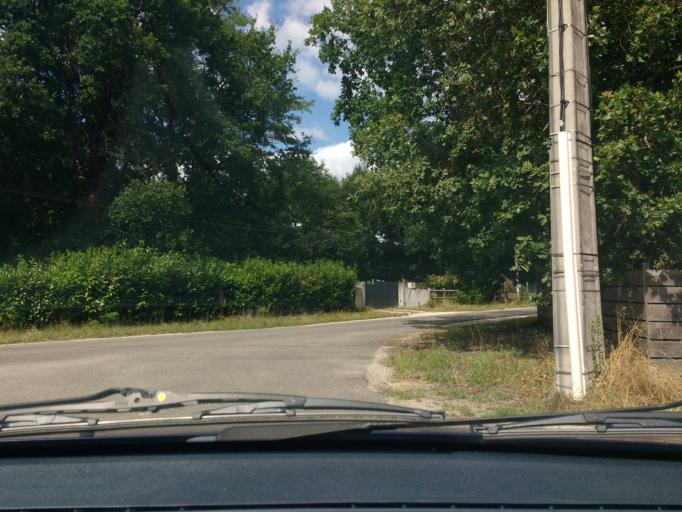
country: FR
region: Aquitaine
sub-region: Departement de la Gironde
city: Salles
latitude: 44.5650
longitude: -0.8411
